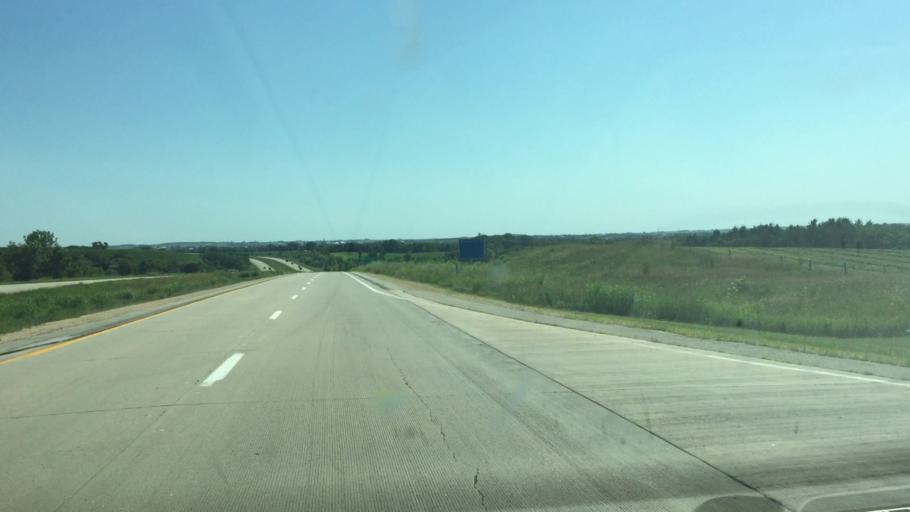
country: US
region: Iowa
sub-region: Jones County
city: Monticello
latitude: 42.2501
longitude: -91.1615
